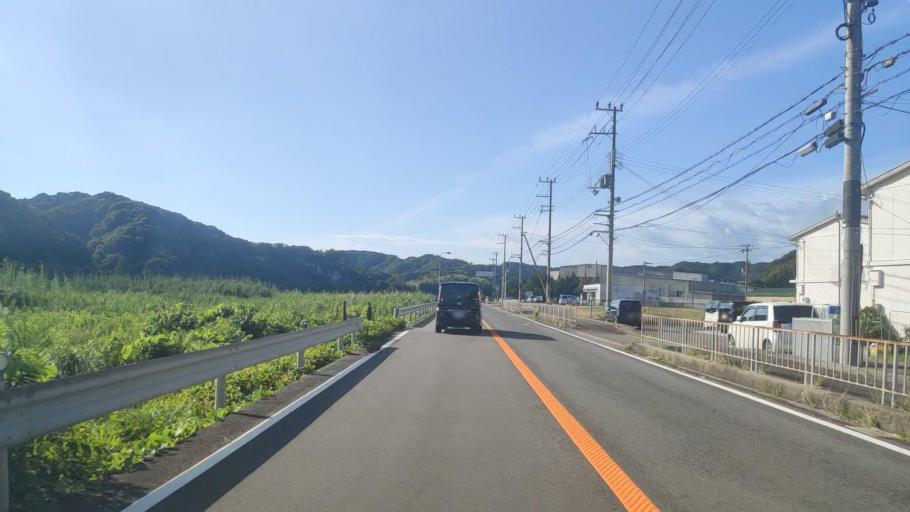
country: JP
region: Wakayama
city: Tanabe
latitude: 33.6587
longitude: 135.4004
